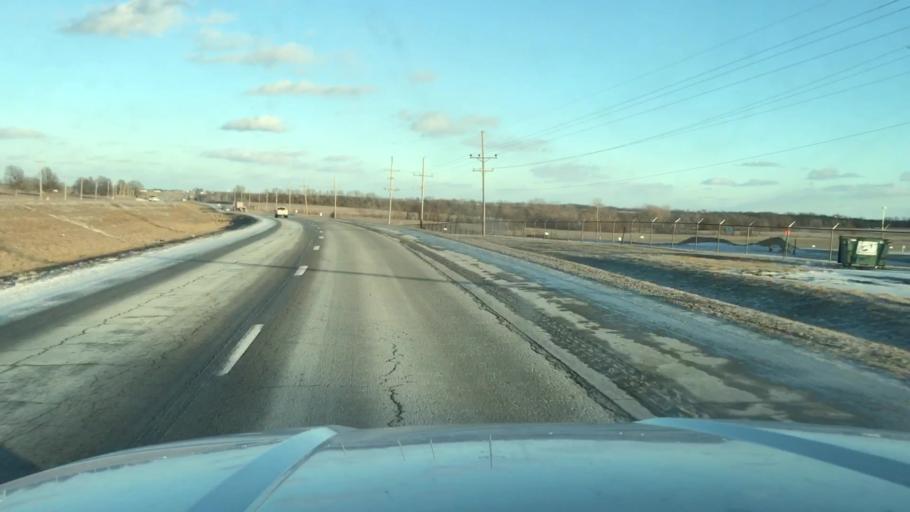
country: US
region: Missouri
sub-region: Clinton County
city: Cameron
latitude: 39.7545
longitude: -94.3372
